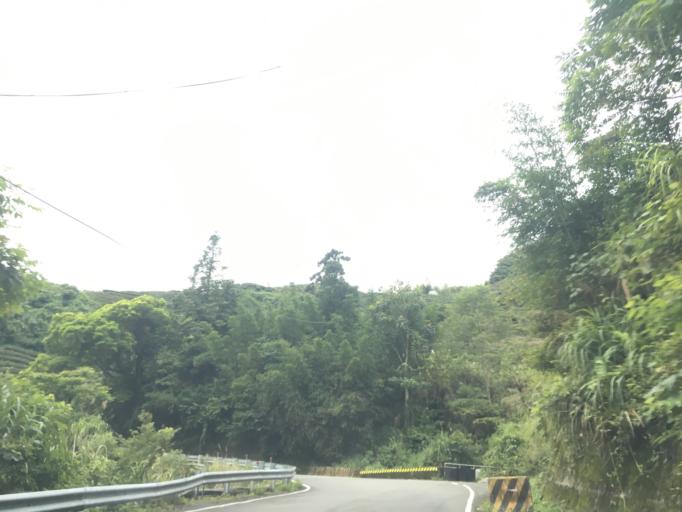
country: TW
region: Taiwan
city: Lugu
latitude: 23.5292
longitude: 120.7062
